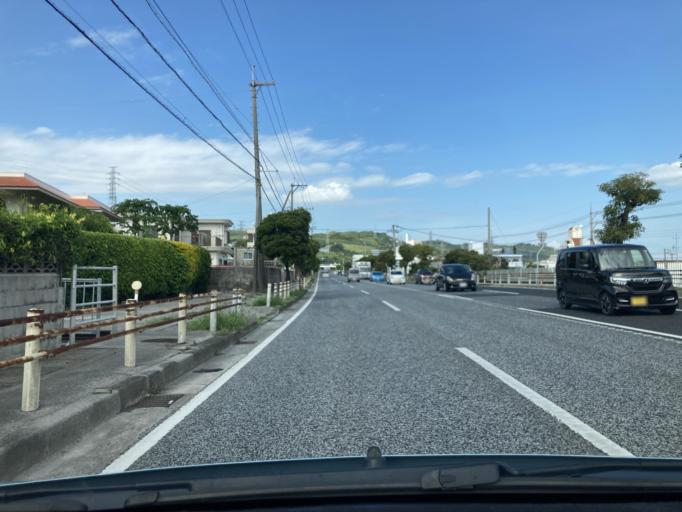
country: JP
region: Okinawa
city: Ginowan
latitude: 26.2647
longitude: 127.7897
